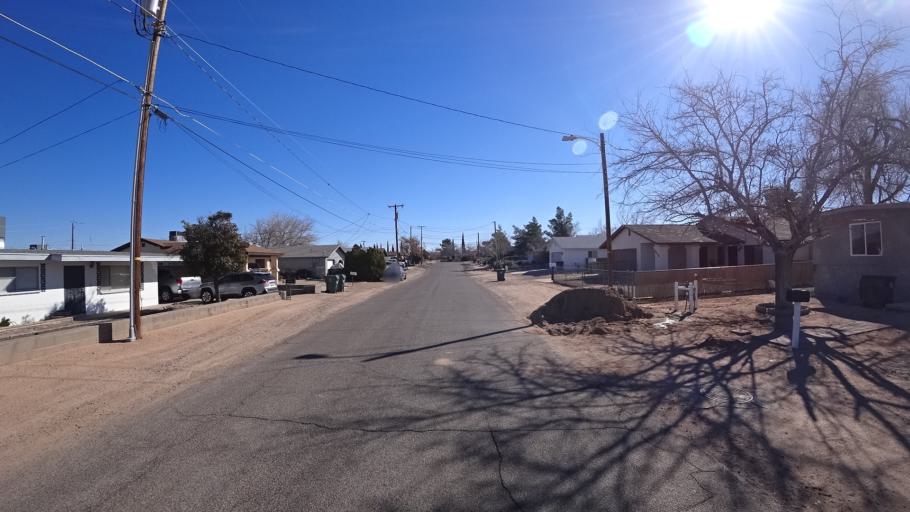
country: US
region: Arizona
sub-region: Mohave County
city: Kingman
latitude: 35.2046
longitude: -114.0261
